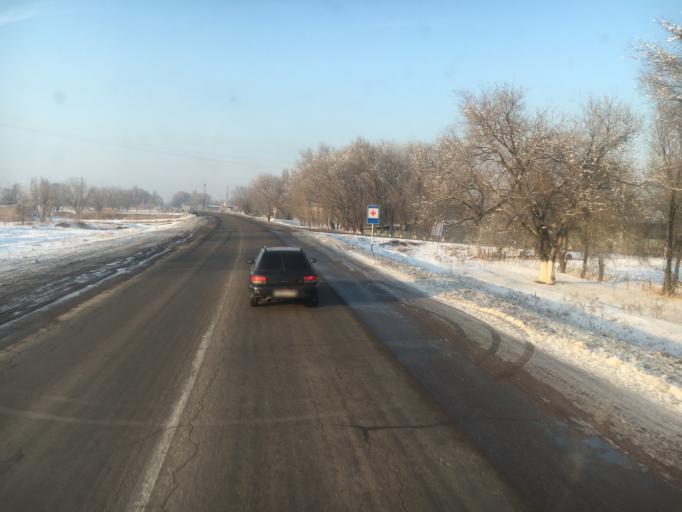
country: KZ
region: Almaty Oblysy
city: Burunday
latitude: 43.3306
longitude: 76.6620
